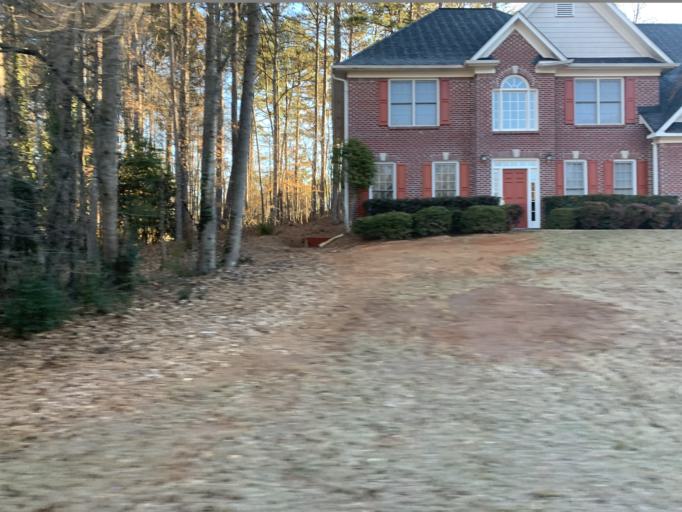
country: US
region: Georgia
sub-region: Gwinnett County
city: Mountain Park
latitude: 33.8634
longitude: -84.1094
